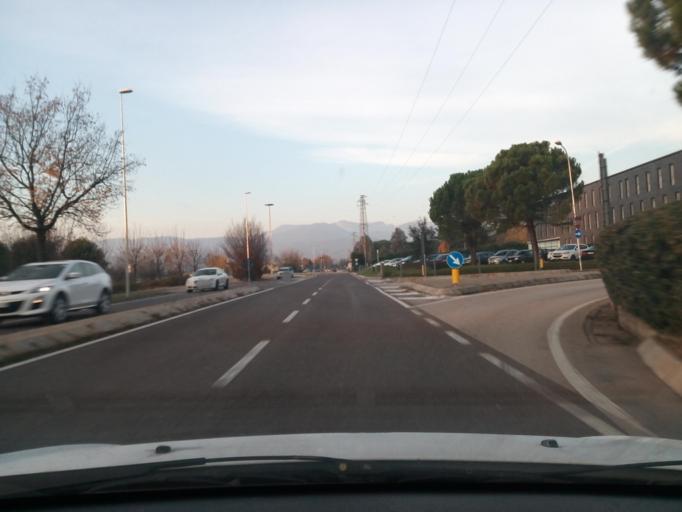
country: IT
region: Veneto
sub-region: Provincia di Vicenza
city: Santorso
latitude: 45.7189
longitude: 11.3957
